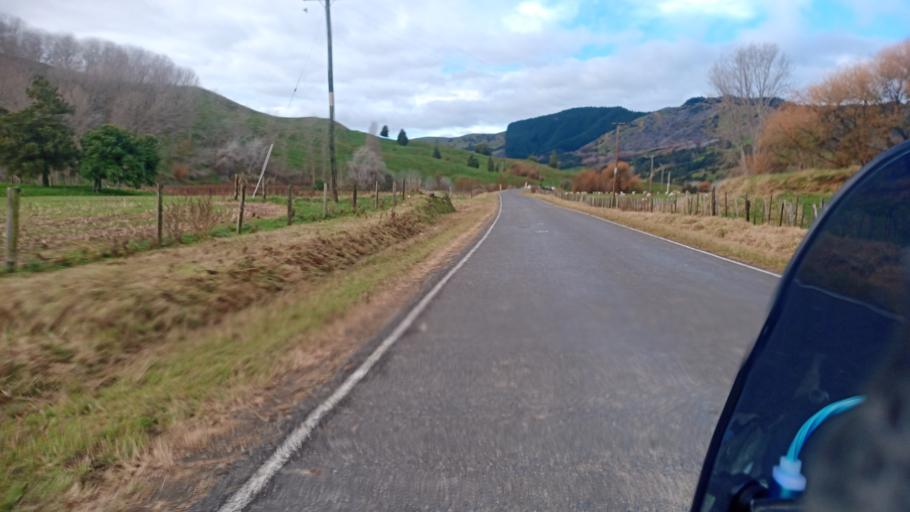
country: NZ
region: Gisborne
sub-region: Gisborne District
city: Gisborne
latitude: -38.4336
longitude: 177.8946
